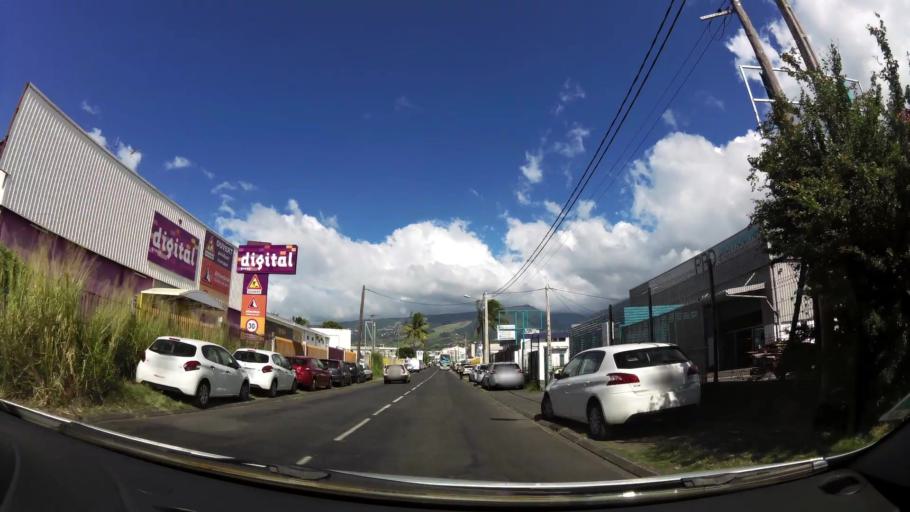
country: RE
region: Reunion
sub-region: Reunion
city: Saint-Denis
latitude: -20.8931
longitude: 55.4958
